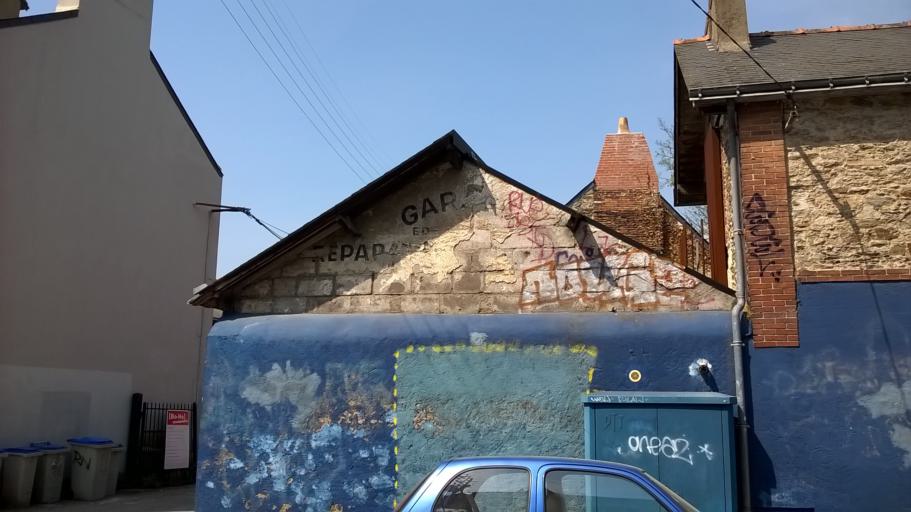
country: FR
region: Pays de la Loire
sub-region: Departement de la Loire-Atlantique
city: Nantes
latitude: 47.2200
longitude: -1.5391
